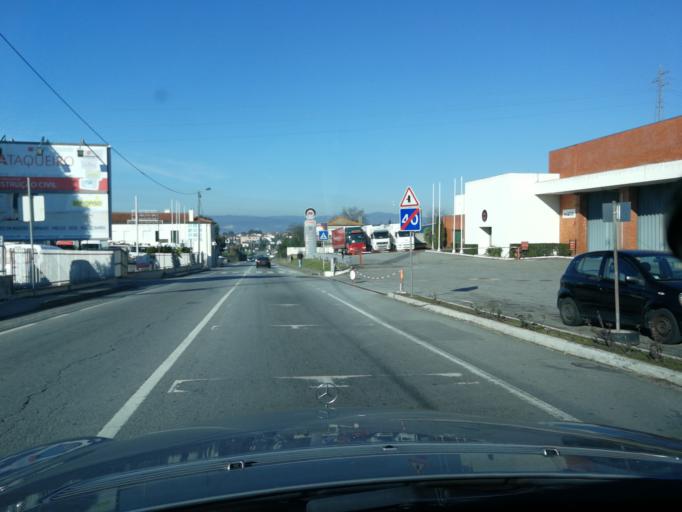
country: PT
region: Braga
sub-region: Braga
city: Braga
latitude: 41.5772
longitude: -8.4258
